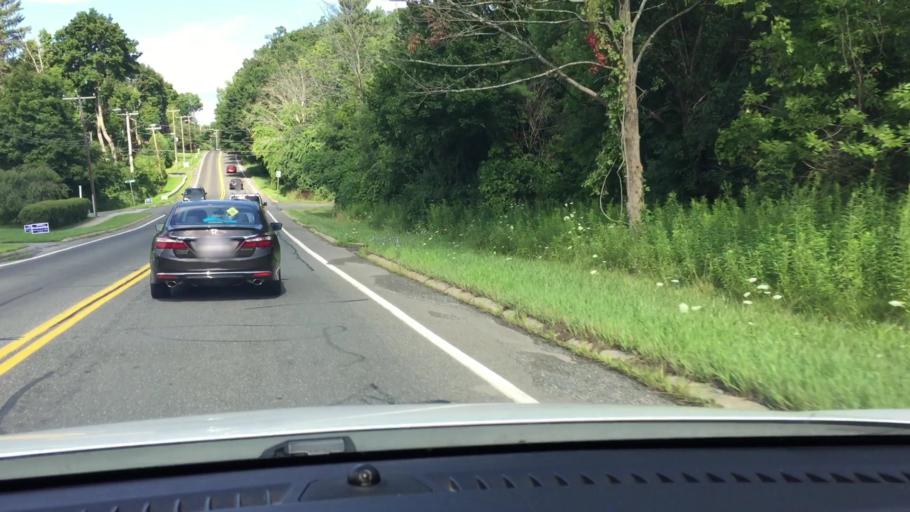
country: US
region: Massachusetts
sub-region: Berkshire County
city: Pittsfield
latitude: 42.4523
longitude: -73.2801
